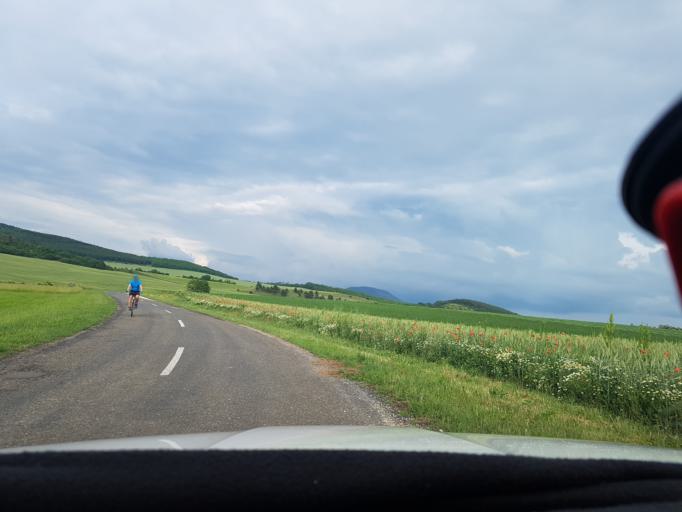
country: HU
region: Komarom-Esztergom
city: Bajna
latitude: 47.7079
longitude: 18.5937
